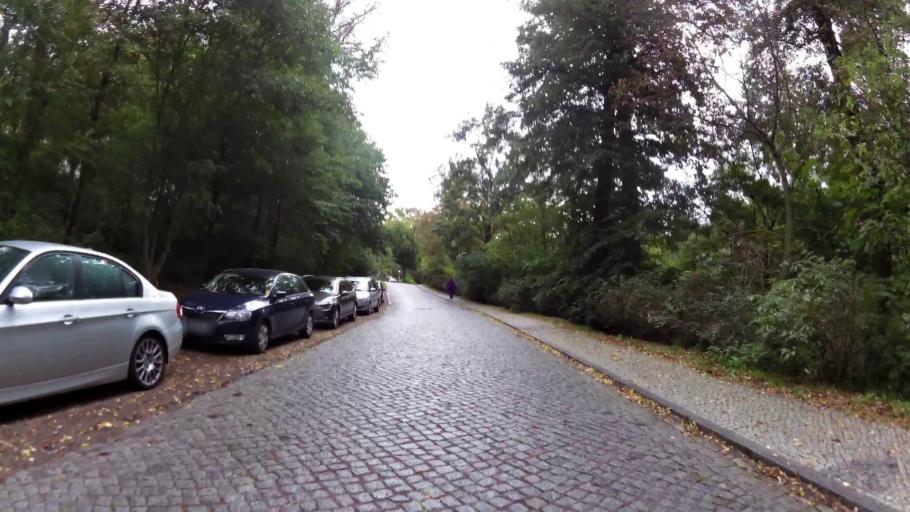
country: DE
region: Thuringia
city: Weimar
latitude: 50.9797
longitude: 11.3352
